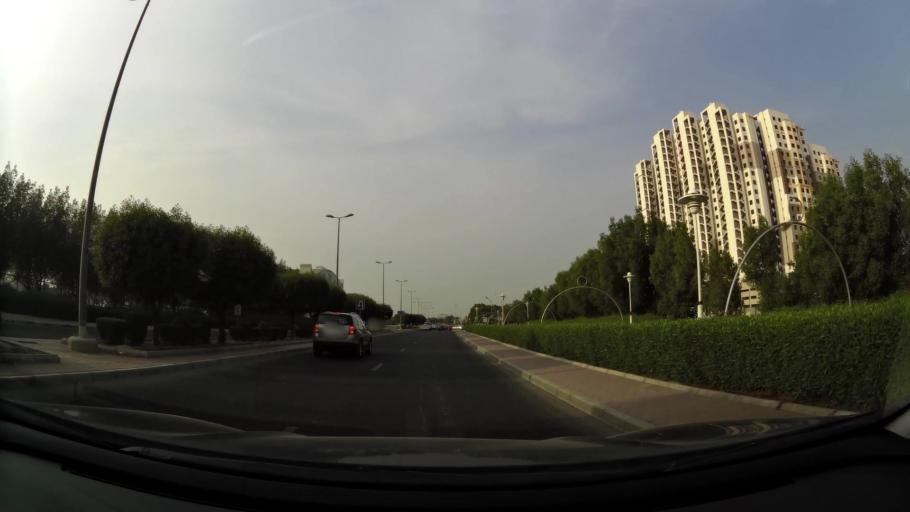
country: KW
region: Mubarak al Kabir
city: Sabah as Salim
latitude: 29.2637
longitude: 48.0770
